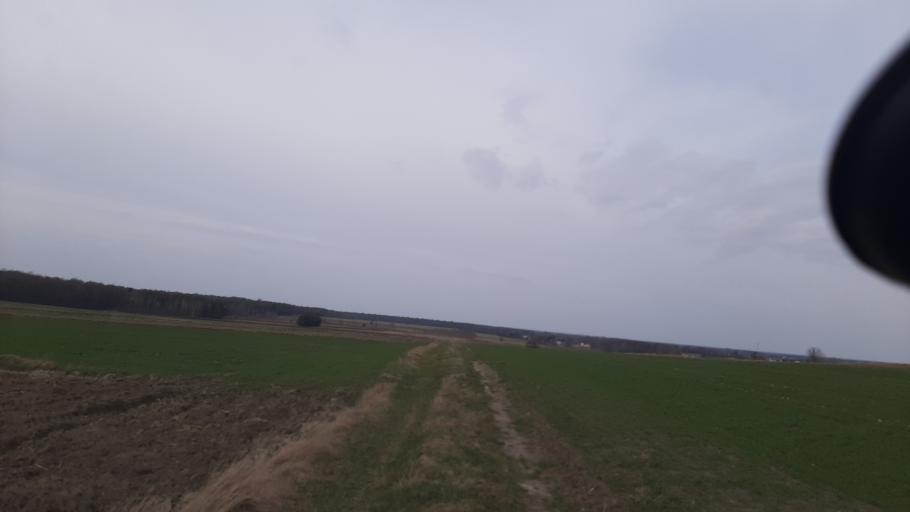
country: PL
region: Lublin Voivodeship
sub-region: Powiat lubelski
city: Jastkow
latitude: 51.3722
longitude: 22.4211
